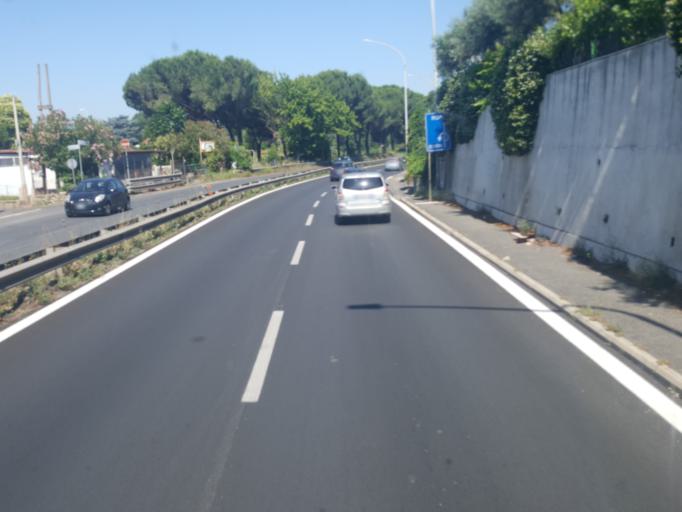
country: IT
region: Latium
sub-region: Citta metropolitana di Roma Capitale
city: Ciampino
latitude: 41.8275
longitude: 12.6246
